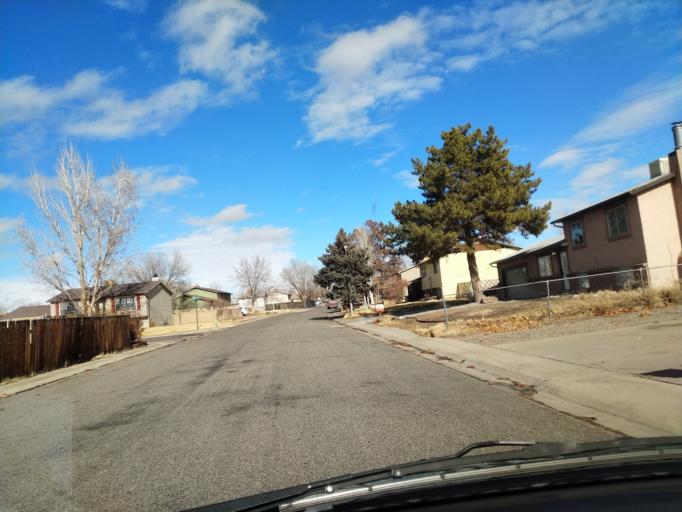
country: US
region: Colorado
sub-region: Mesa County
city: Fruitvale
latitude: 39.0746
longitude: -108.4878
